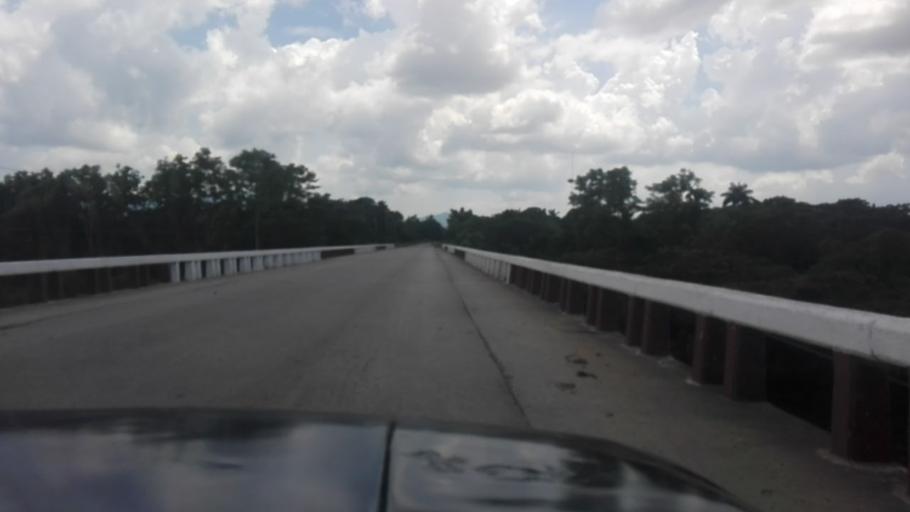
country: CU
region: Granma
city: Bartolome Maso
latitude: 20.1470
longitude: -76.9607
